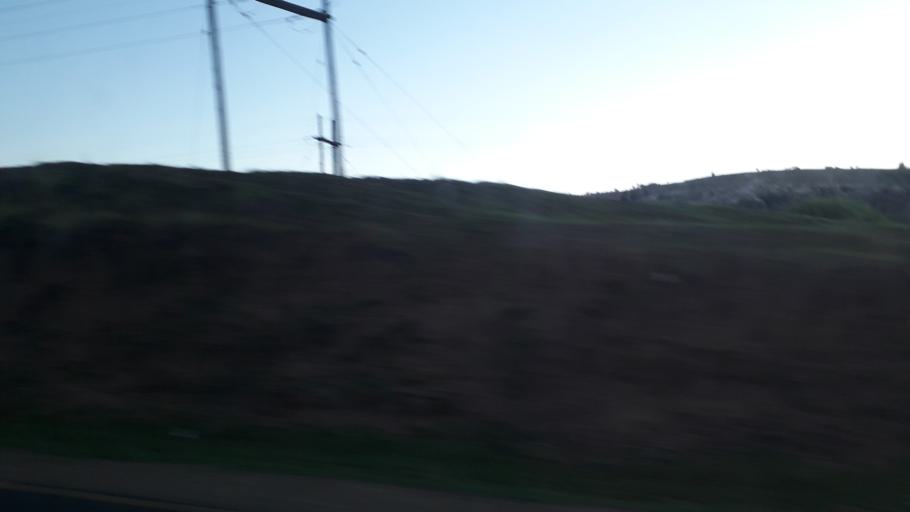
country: LS
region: Butha-Buthe
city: Butha-Buthe
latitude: -28.7320
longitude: 28.4003
